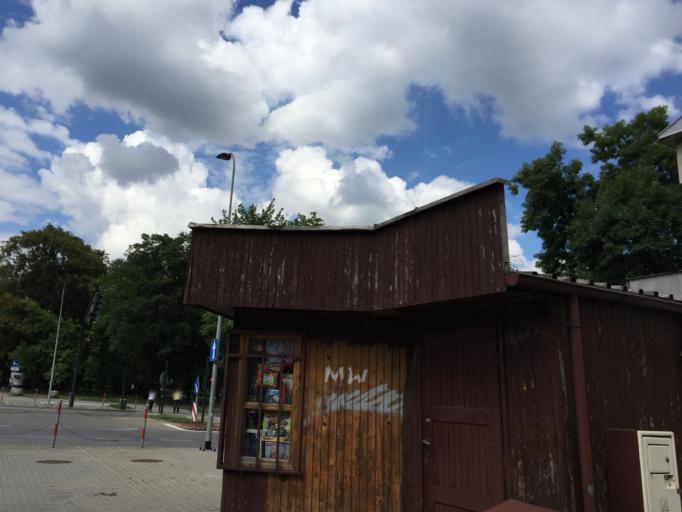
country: PL
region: Lesser Poland Voivodeship
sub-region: Powiat wielicki
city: Kokotow
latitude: 50.0733
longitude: 20.0427
